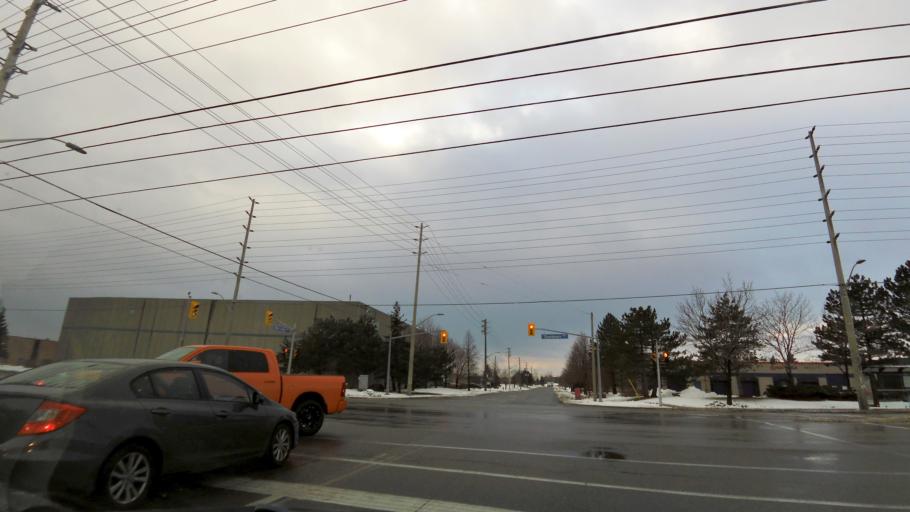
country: CA
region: Ontario
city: Mississauga
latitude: 43.6601
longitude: -79.6771
